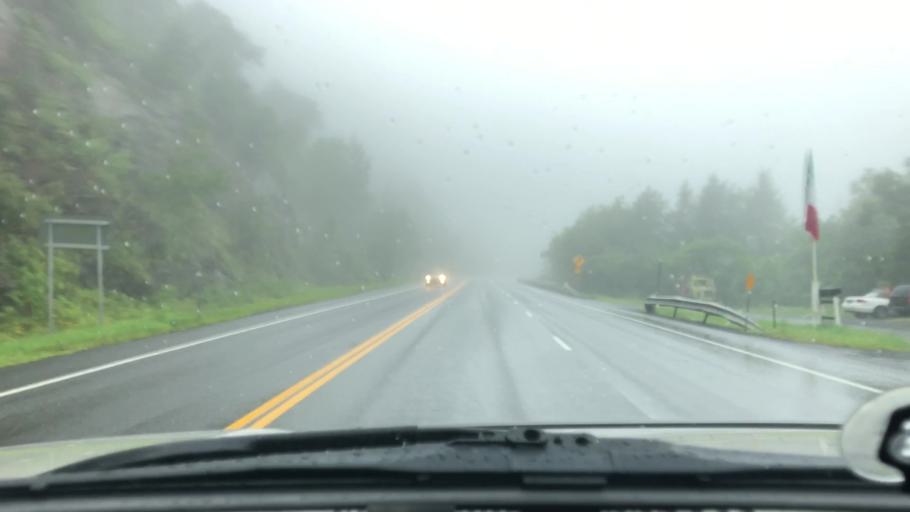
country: US
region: New York
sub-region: Greene County
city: Cairo
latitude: 42.3352
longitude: -74.1464
